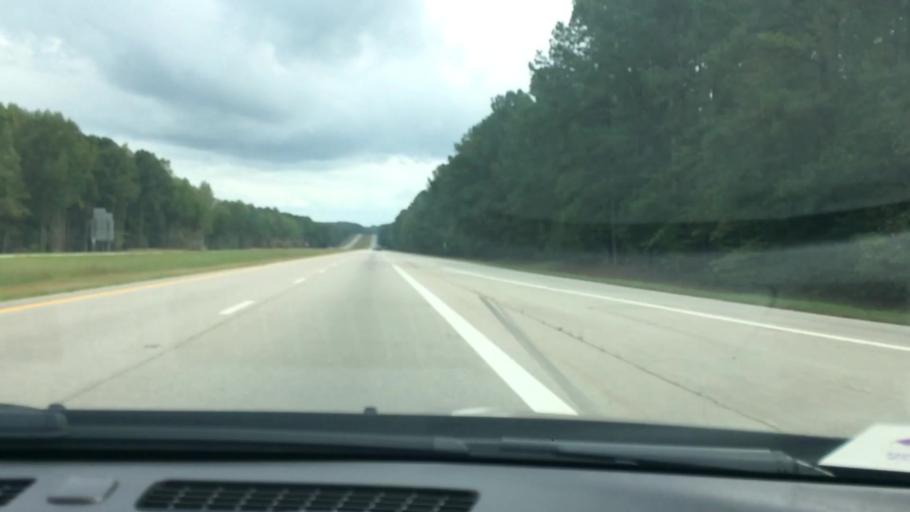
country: US
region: North Carolina
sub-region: Wake County
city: Zebulon
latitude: 35.8196
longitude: -78.2652
